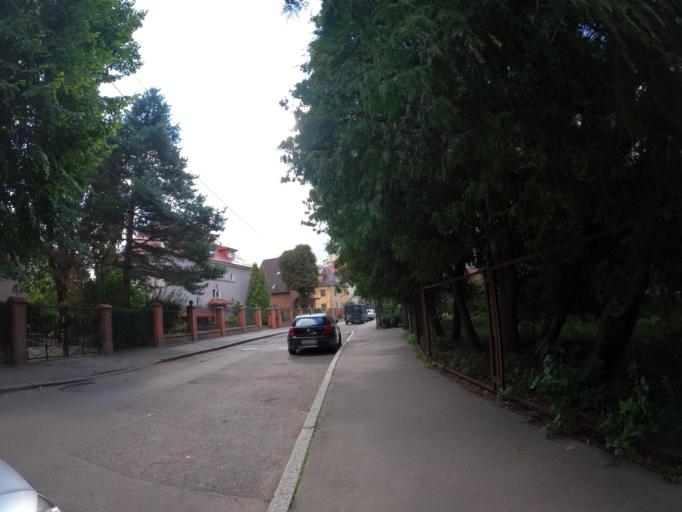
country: RU
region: Kaliningrad
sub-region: Gorod Kaliningrad
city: Kaliningrad
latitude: 54.7305
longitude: 20.4764
